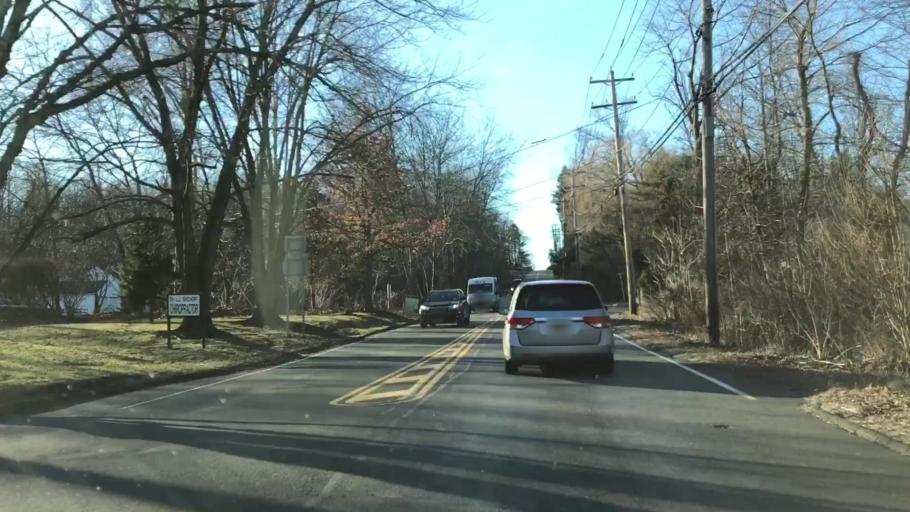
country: US
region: New York
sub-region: Rockland County
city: New Hempstead
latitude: 41.1492
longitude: -74.0283
